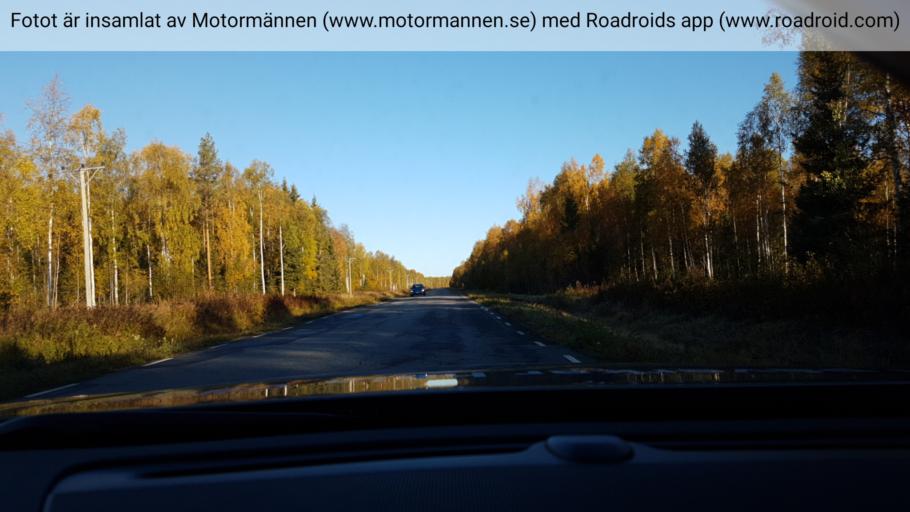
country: SE
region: Norrbotten
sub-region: Bodens Kommun
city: Boden
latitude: 65.8983
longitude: 21.6743
